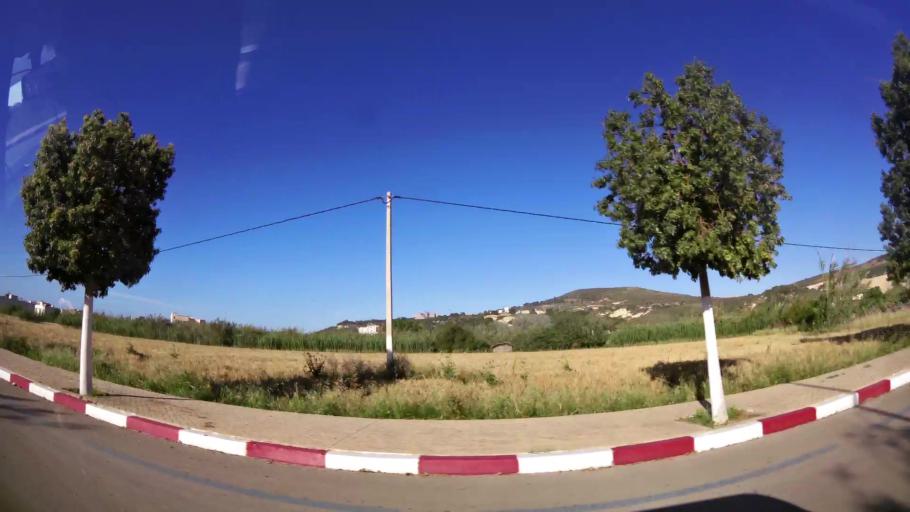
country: MA
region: Oriental
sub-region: Berkane-Taourirt
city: Madagh
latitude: 35.0694
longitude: -2.2170
